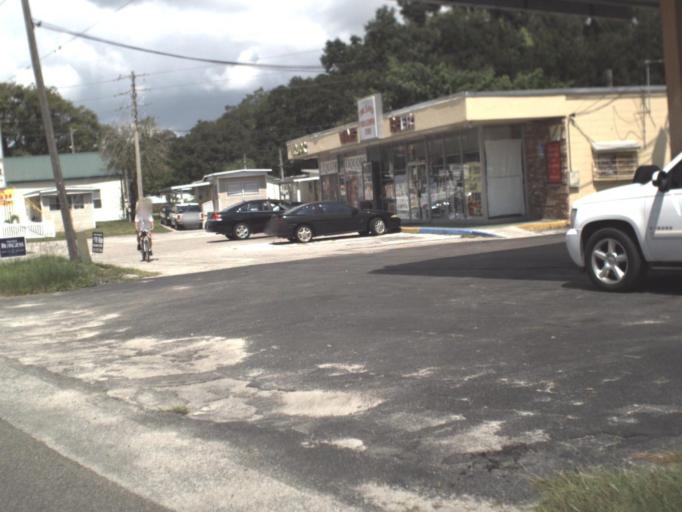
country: US
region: Florida
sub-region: Pasco County
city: Zephyrhills
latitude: 28.2302
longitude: -82.1896
